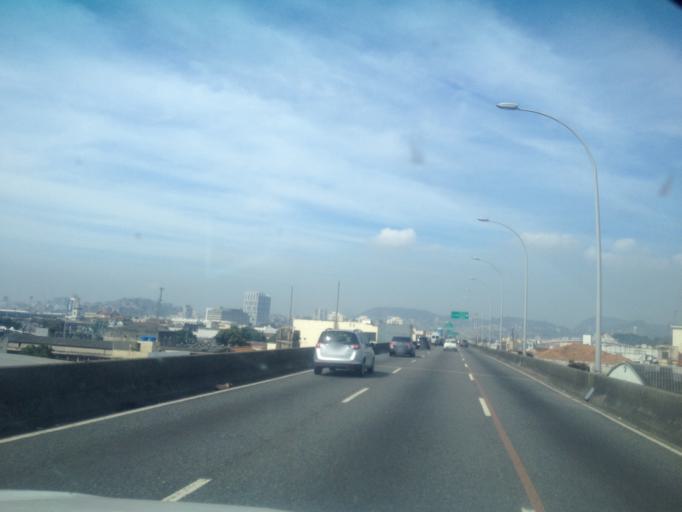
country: BR
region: Rio de Janeiro
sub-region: Rio De Janeiro
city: Rio de Janeiro
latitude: -22.8872
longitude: -43.2258
